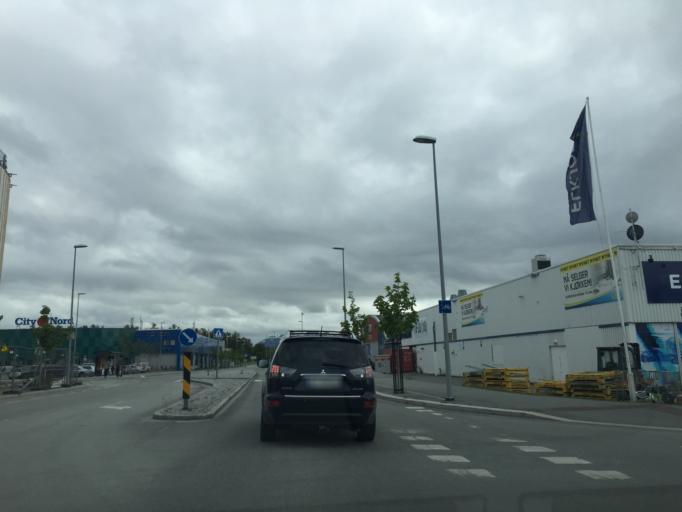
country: NO
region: Nordland
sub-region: Bodo
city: Bodo
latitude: 67.2777
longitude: 14.4192
